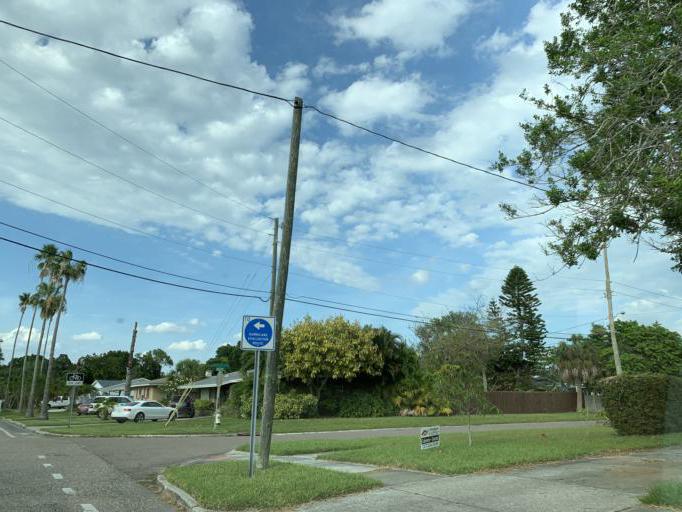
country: US
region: Florida
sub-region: Pinellas County
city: Gandy
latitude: 27.8093
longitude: -82.6020
